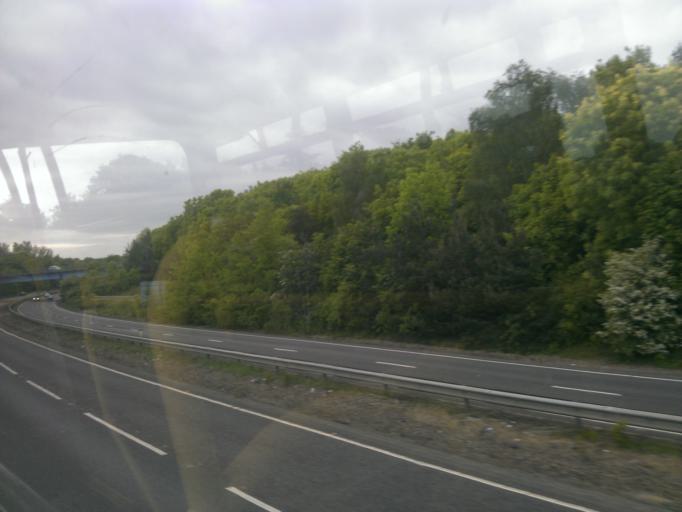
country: GB
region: England
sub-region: Essex
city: Colchester
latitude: 51.9257
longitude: 0.9392
